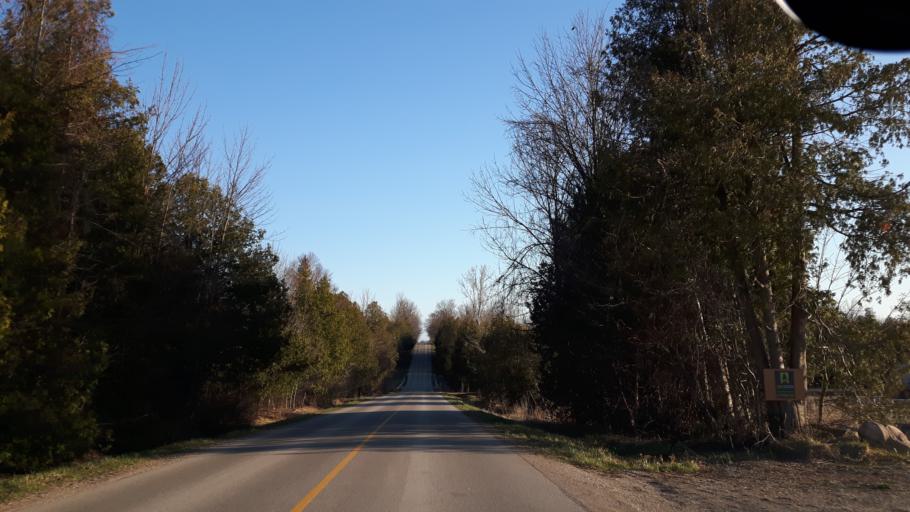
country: CA
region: Ontario
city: Goderich
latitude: 43.6590
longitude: -81.6847
